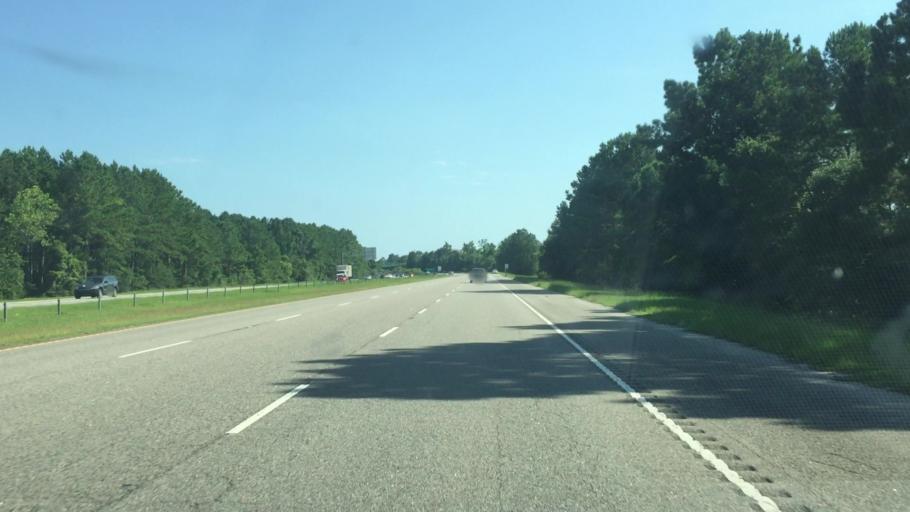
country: US
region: South Carolina
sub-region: Horry County
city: North Myrtle Beach
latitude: 33.8024
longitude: -78.7792
